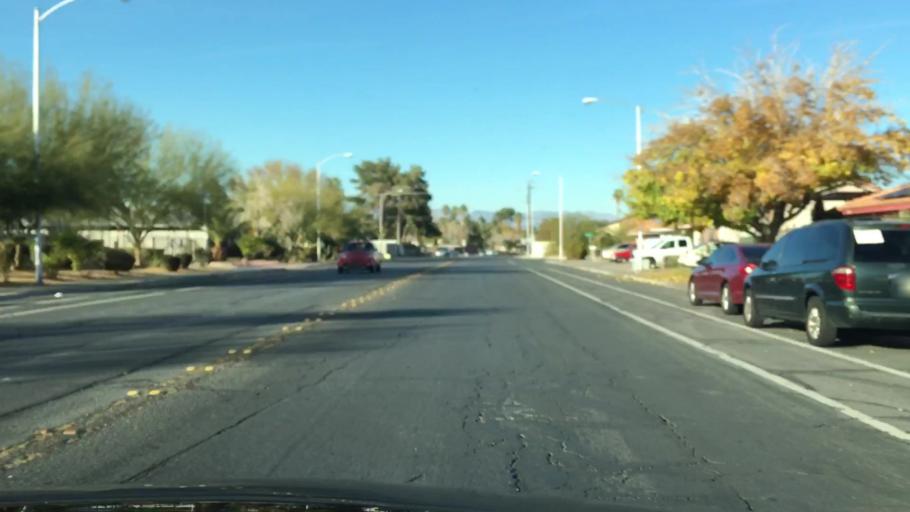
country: US
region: Nevada
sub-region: Clark County
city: Paradise
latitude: 36.1029
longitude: -115.1280
